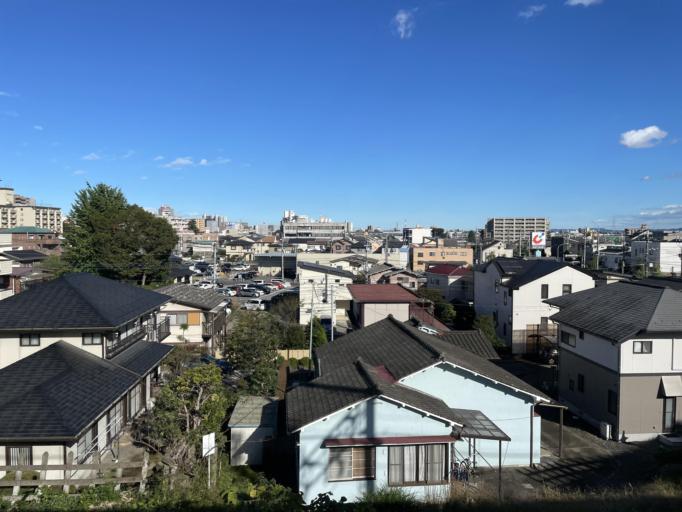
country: JP
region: Tochigi
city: Utsunomiya-shi
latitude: 36.5520
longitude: 139.8819
